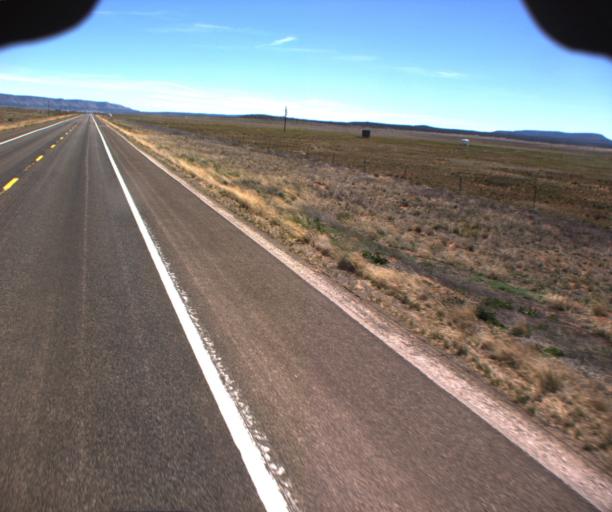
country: US
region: Arizona
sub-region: Mohave County
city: Peach Springs
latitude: 35.4693
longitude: -113.1235
